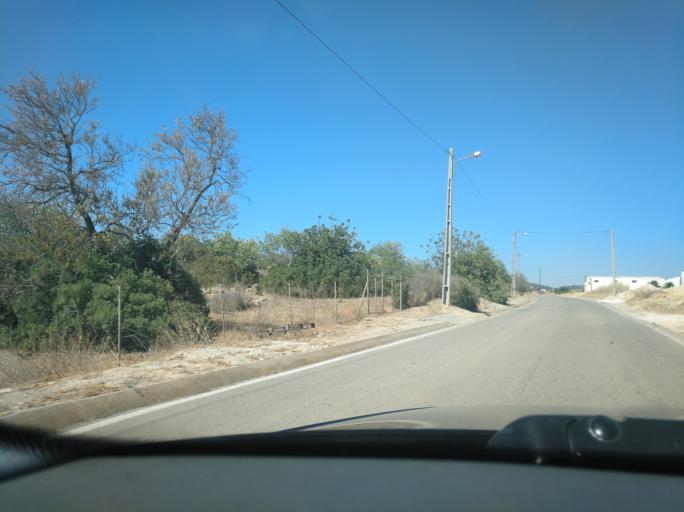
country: PT
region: Faro
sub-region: Faro
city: Faro
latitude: 37.0680
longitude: -7.8959
